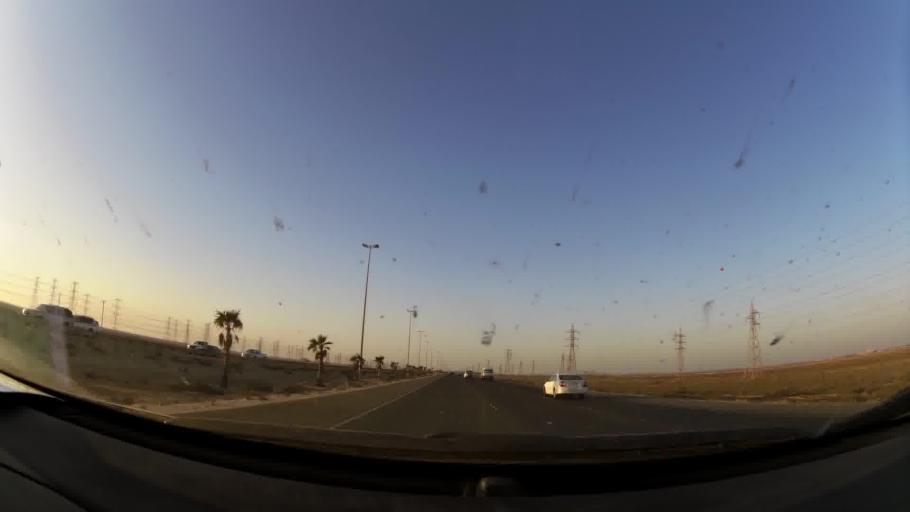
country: KW
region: Al Ahmadi
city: Al Fahahil
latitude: 28.8278
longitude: 48.2564
